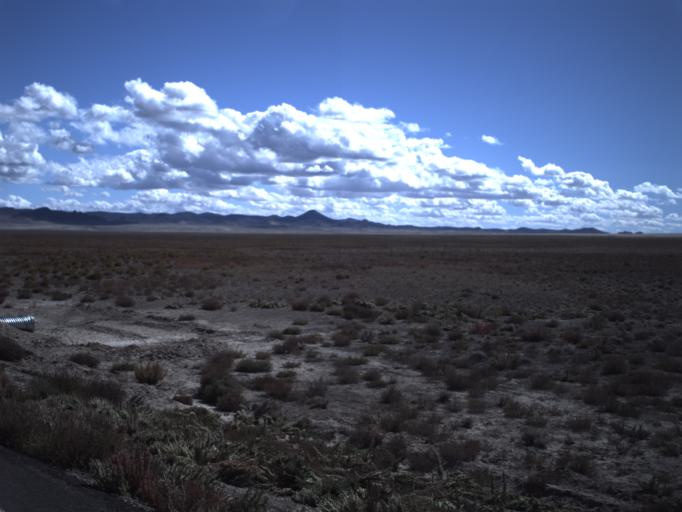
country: US
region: Utah
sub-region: Beaver County
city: Milford
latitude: 38.4794
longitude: -113.4344
